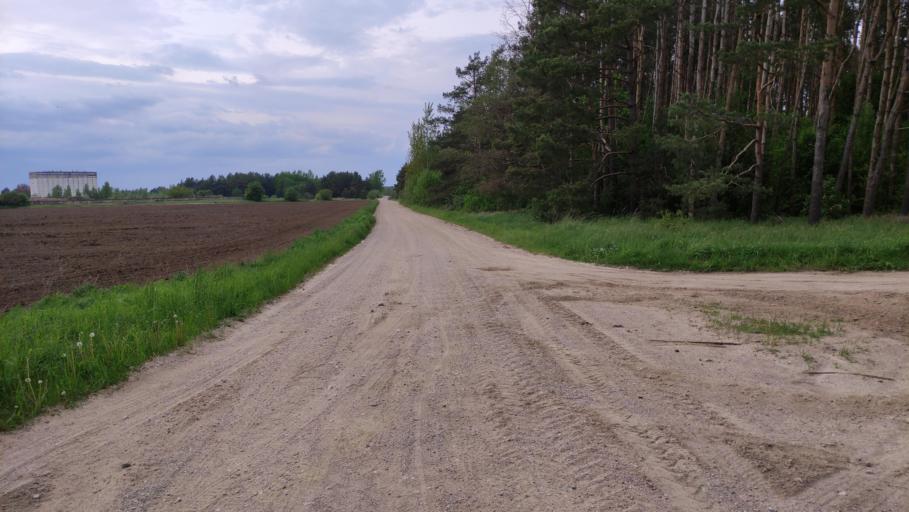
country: LT
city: Prienai
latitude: 54.5021
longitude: 23.9330
